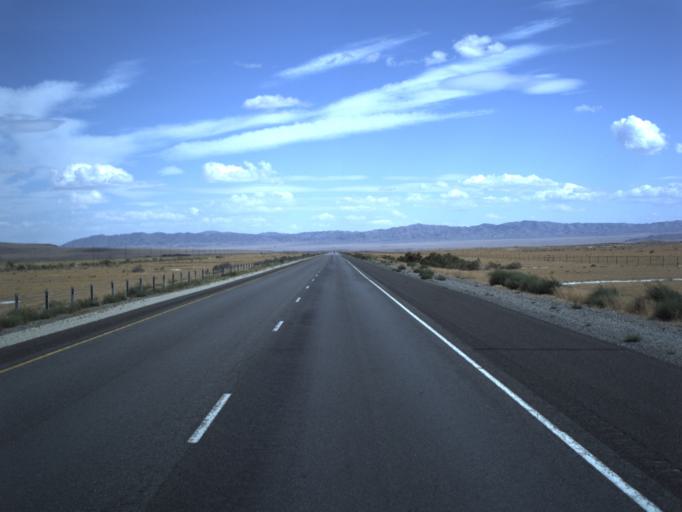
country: US
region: Utah
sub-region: Tooele County
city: Grantsville
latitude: 40.7259
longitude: -113.2156
